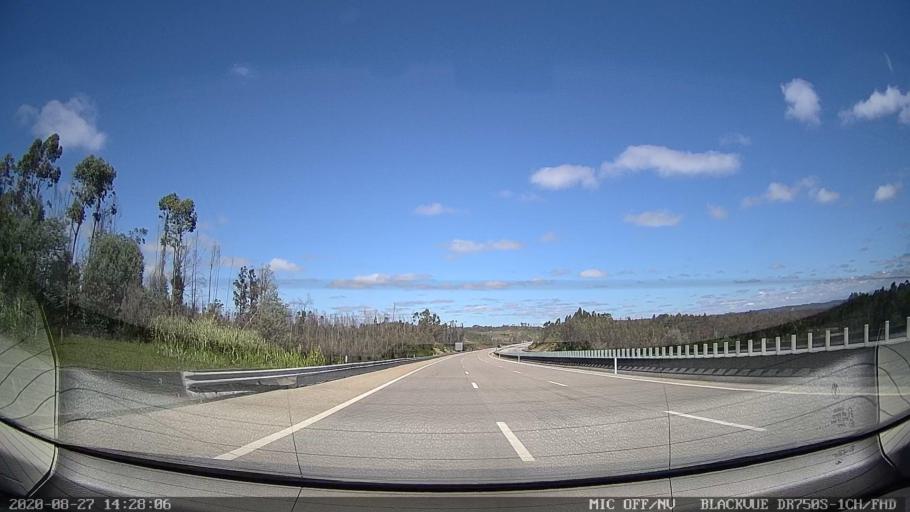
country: PT
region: Coimbra
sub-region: Figueira da Foz
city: Lavos
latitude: 40.0643
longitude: -8.7959
